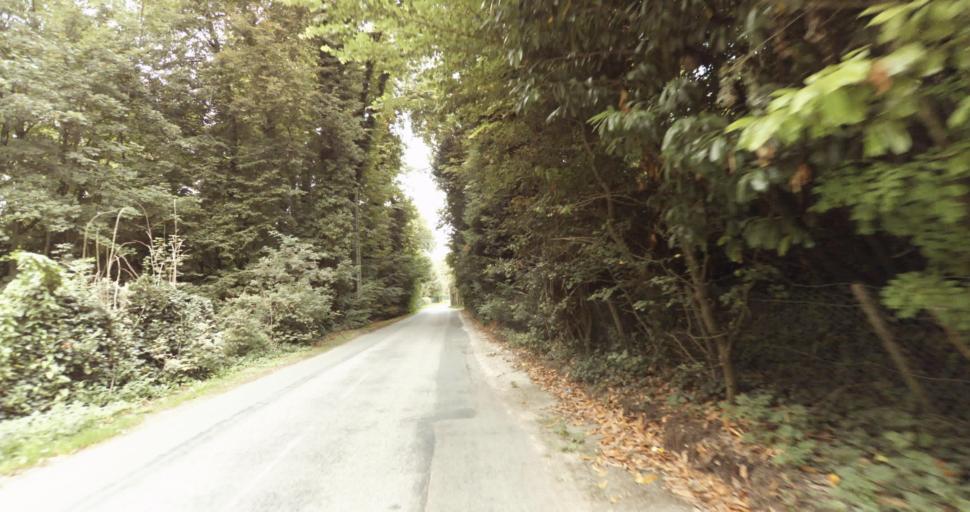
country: FR
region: Centre
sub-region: Departement d'Eure-et-Loir
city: Vert-en-Drouais
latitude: 48.7663
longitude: 1.3082
